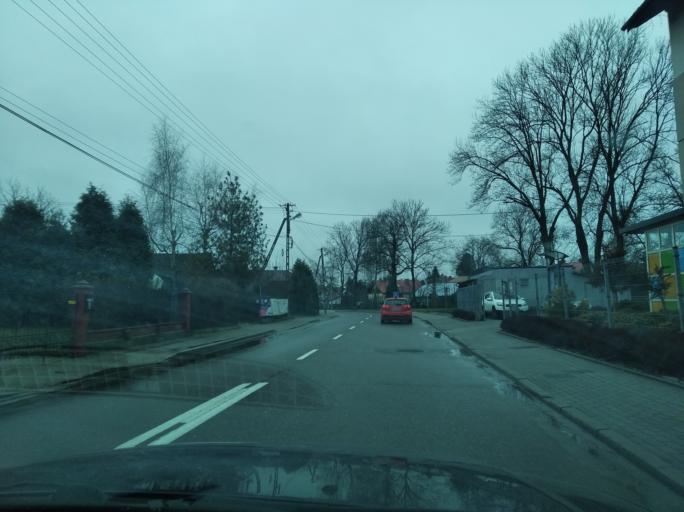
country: PL
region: Subcarpathian Voivodeship
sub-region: Rzeszow
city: Rzeszow
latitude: 50.0592
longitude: 21.9998
